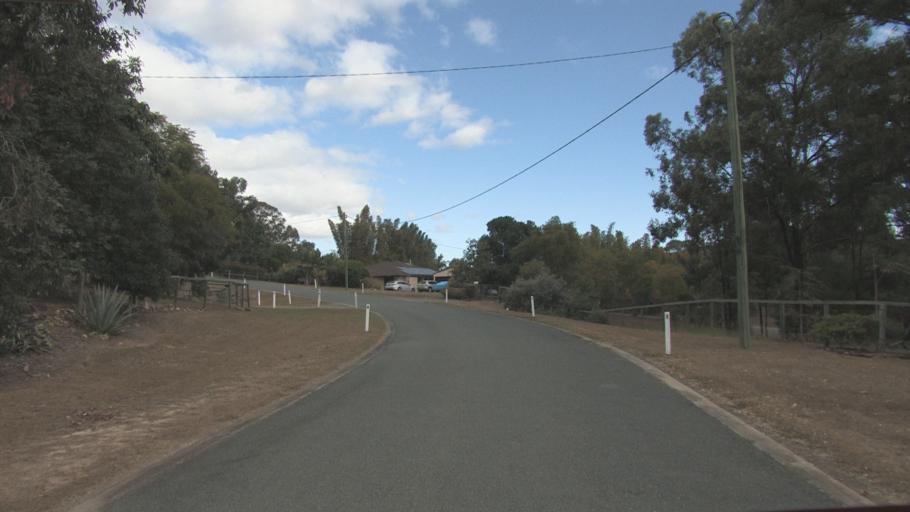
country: AU
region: Queensland
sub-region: Logan
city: Cedar Vale
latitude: -27.8854
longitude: 153.0134
